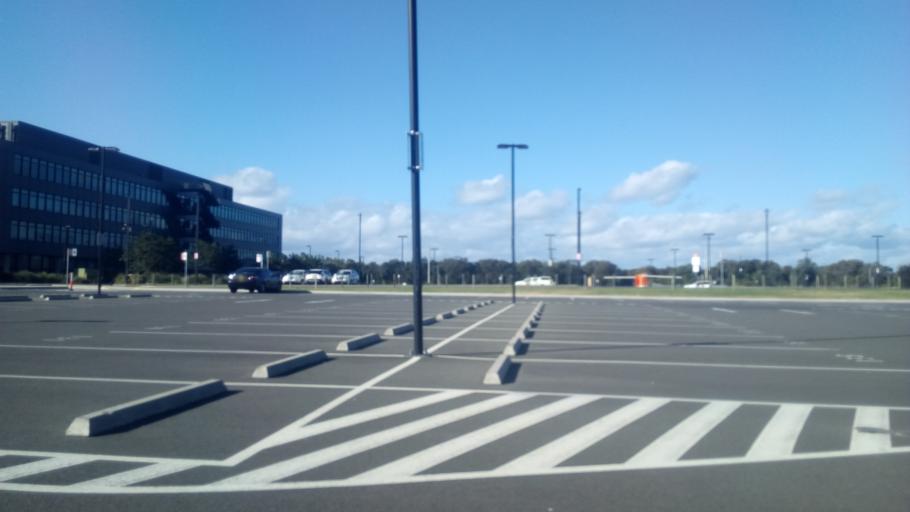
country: AU
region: New South Wales
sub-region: Wollongong
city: Fairy Meadow
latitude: -34.4038
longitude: 150.8971
